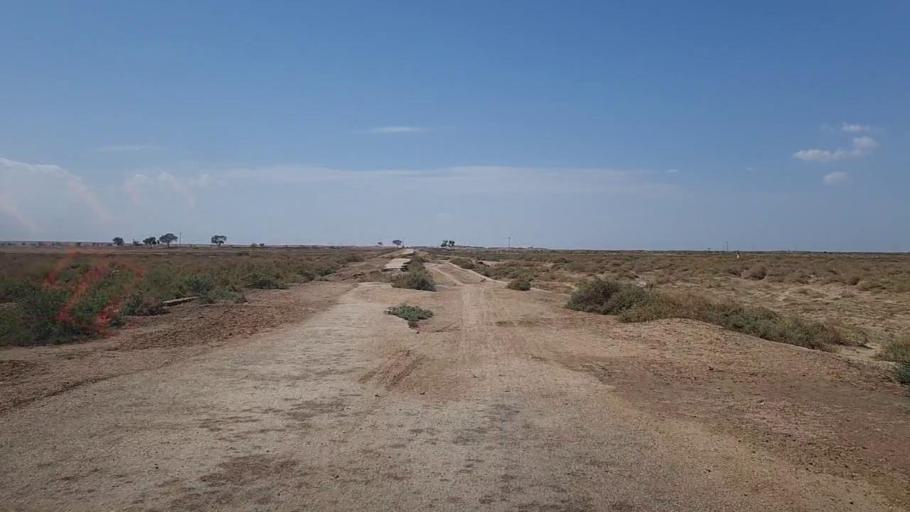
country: PK
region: Sindh
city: Sehwan
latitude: 26.3573
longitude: 67.6701
